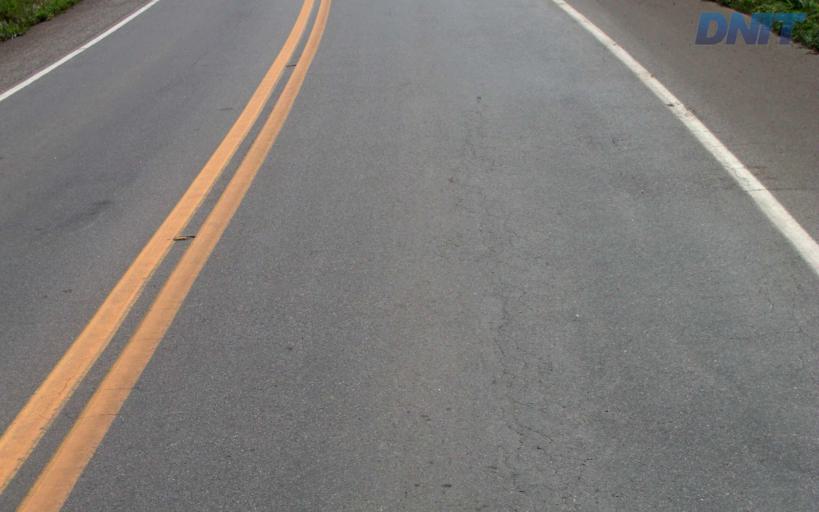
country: BR
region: Minas Gerais
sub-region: Belo Oriente
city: Belo Oriente
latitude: -19.1363
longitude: -42.2141
